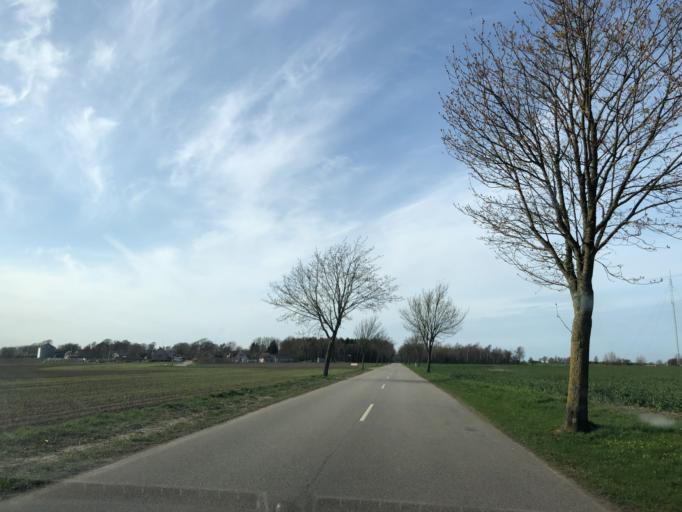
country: DK
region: Zealand
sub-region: Stevns Kommune
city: Store Heddinge
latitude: 55.2939
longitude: 12.4452
